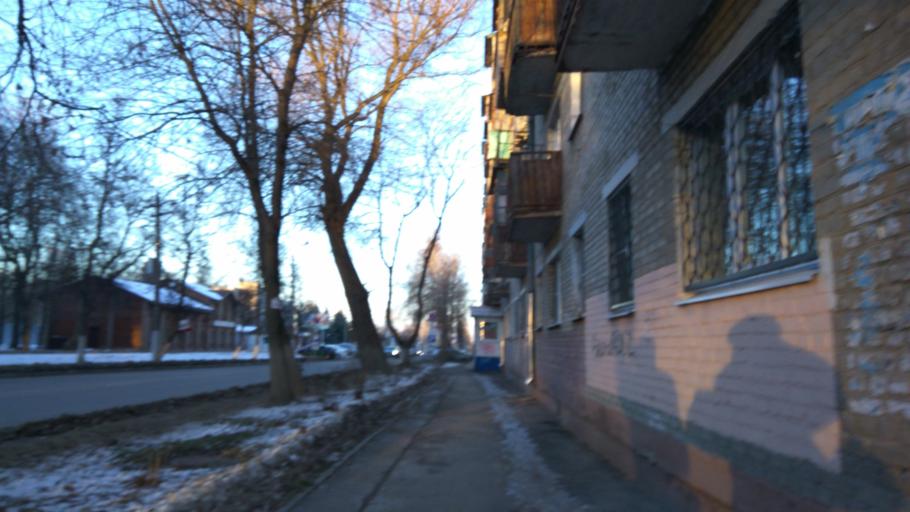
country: RU
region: Tula
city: Tula
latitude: 54.1778
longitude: 37.5969
